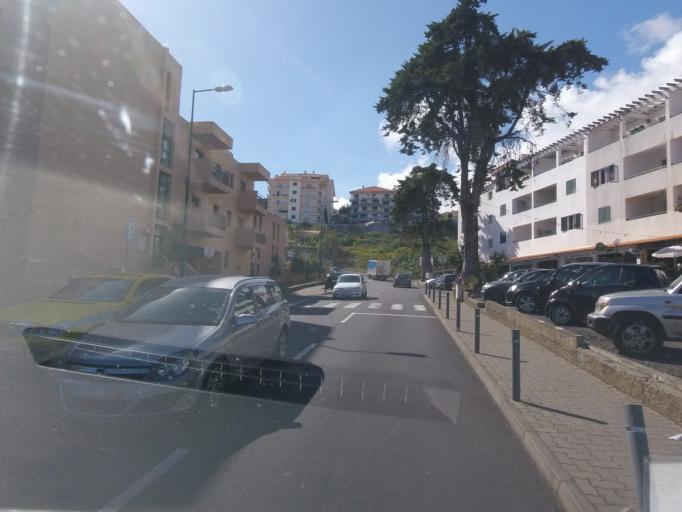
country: PT
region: Madeira
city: Canico
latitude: 32.6442
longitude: -16.8534
